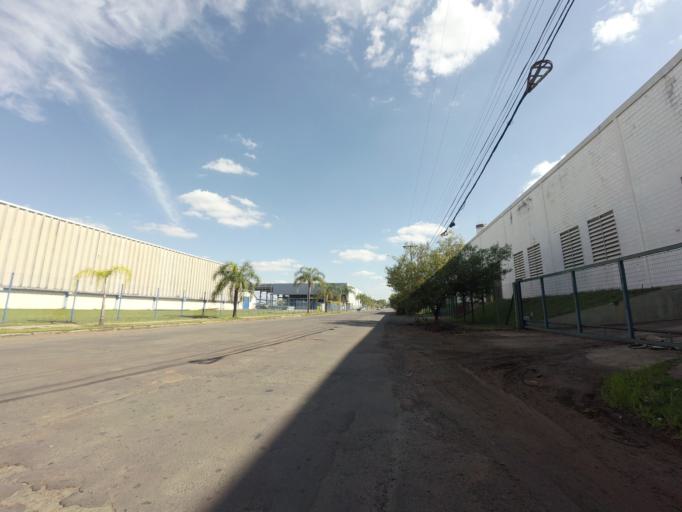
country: BR
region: Sao Paulo
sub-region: Piracicaba
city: Piracicaba
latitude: -22.7261
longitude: -47.5954
